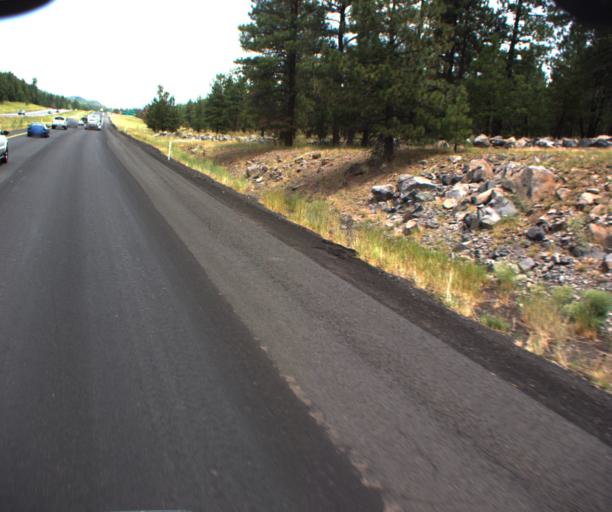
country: US
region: Arizona
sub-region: Coconino County
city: Mountainaire
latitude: 34.9740
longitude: -111.6851
